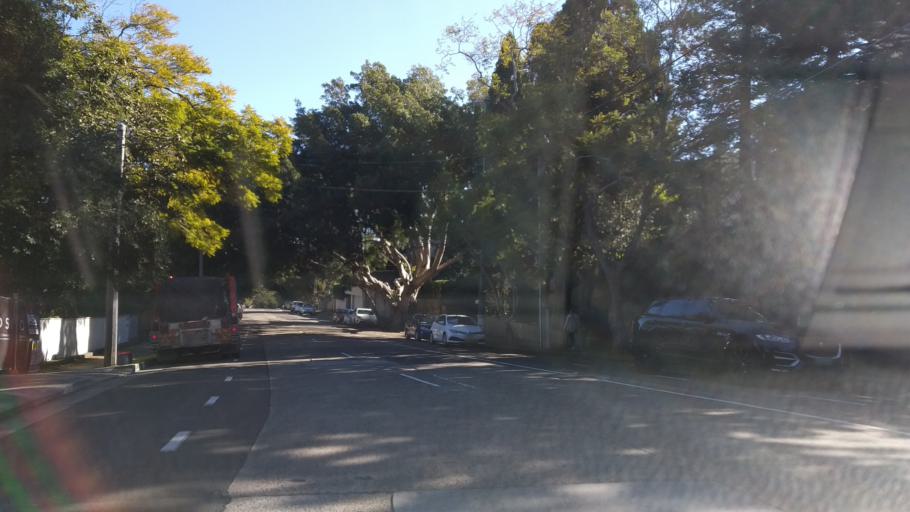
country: AU
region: New South Wales
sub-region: Woollahra
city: Bellevue Hill
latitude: -33.8794
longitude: 151.2483
